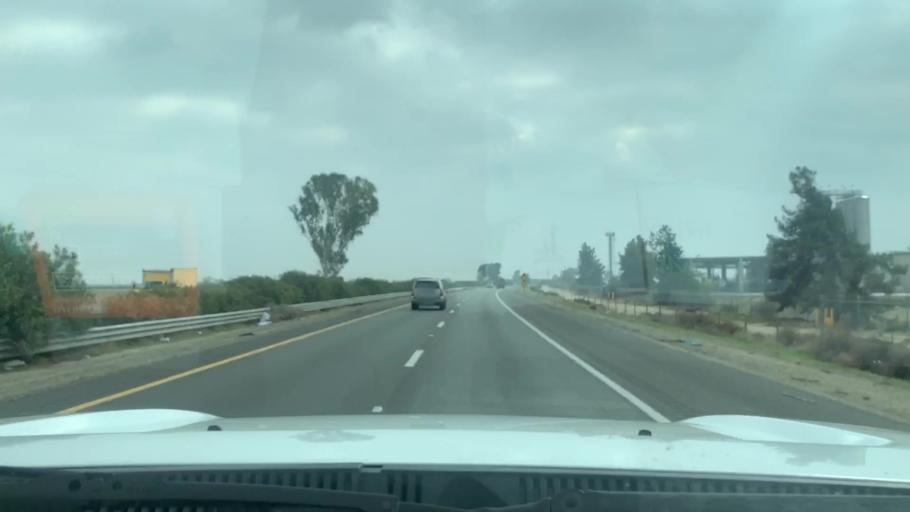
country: US
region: California
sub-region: Tulare County
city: Tipton
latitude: 36.1333
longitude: -119.3260
